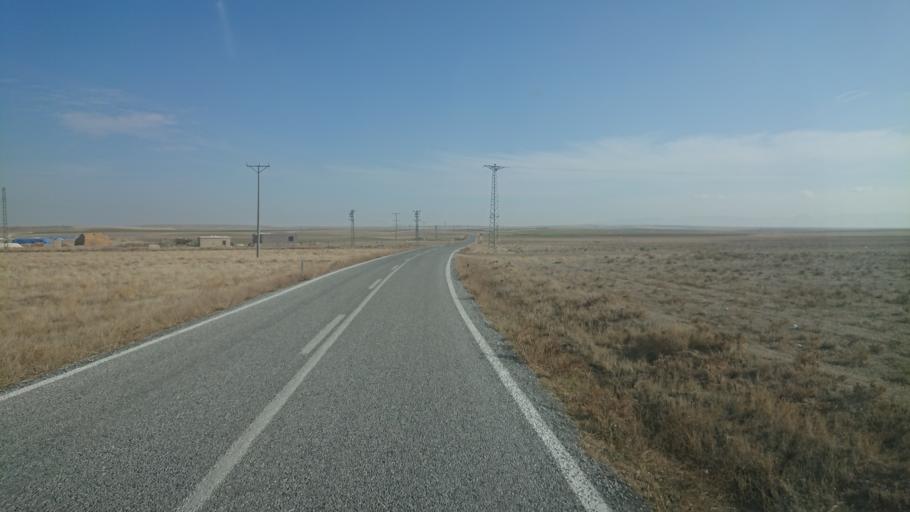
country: TR
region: Aksaray
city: Sultanhani
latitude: 38.0359
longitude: 33.6043
